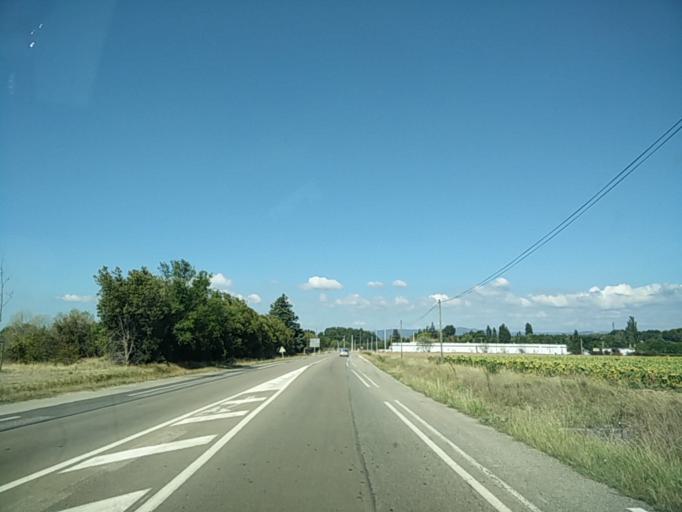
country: FR
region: Rhone-Alpes
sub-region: Departement de la Drome
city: Montboucher-sur-Jabron
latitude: 44.5552
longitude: 4.8506
